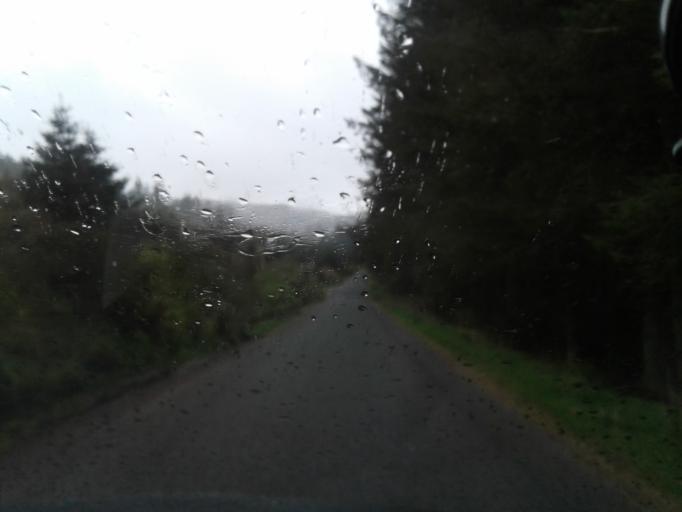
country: IE
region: Leinster
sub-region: Wicklow
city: Enniskerry
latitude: 53.1181
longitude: -6.2684
